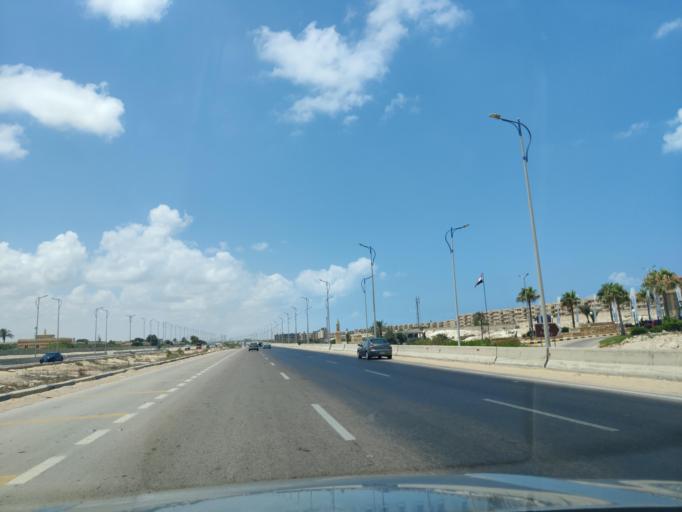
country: EG
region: Muhafazat Matruh
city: Al `Alamayn
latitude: 30.9245
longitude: 29.4636
